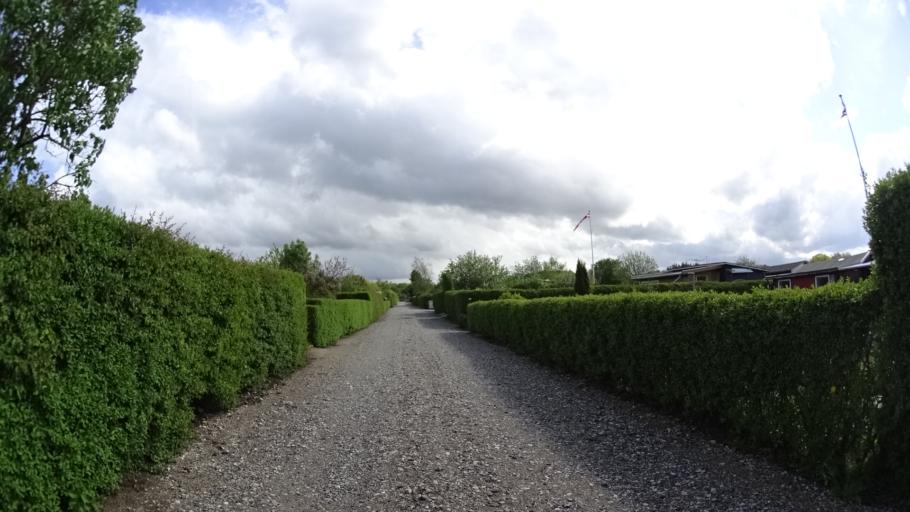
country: DK
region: Central Jutland
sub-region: Arhus Kommune
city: Stavtrup
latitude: 56.1370
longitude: 10.1440
